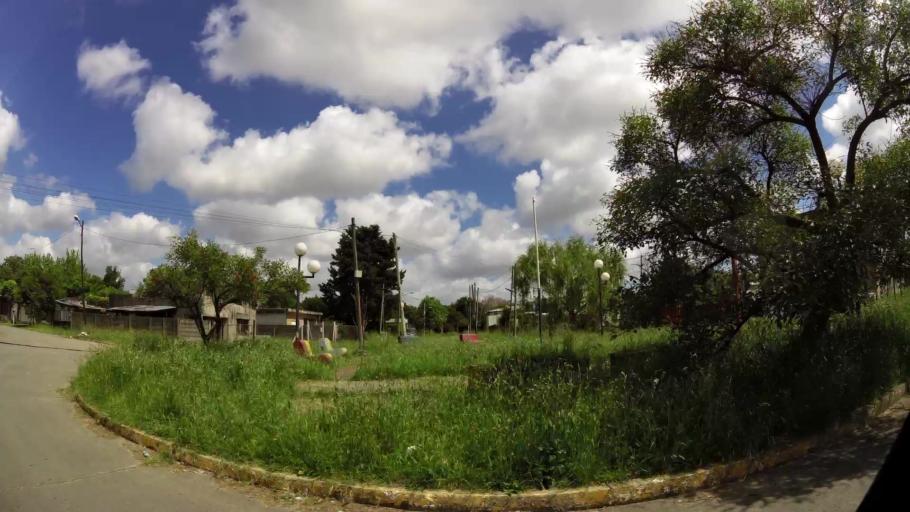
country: AR
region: Buenos Aires
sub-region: Partido de Quilmes
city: Quilmes
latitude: -34.8373
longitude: -58.1796
